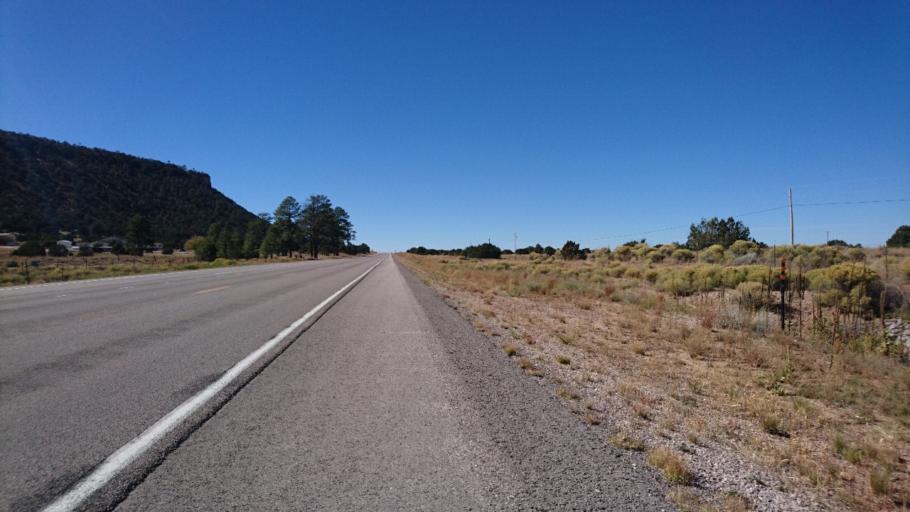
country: US
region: New Mexico
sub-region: McKinley County
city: Thoreau
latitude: 35.0446
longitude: -108.3026
